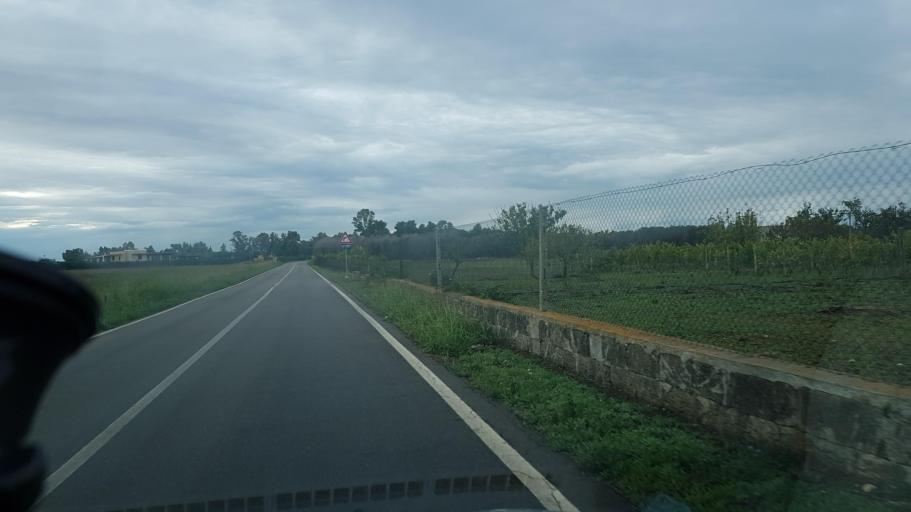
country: IT
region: Apulia
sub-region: Provincia di Lecce
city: Carmiano
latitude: 40.3540
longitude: 18.0286
